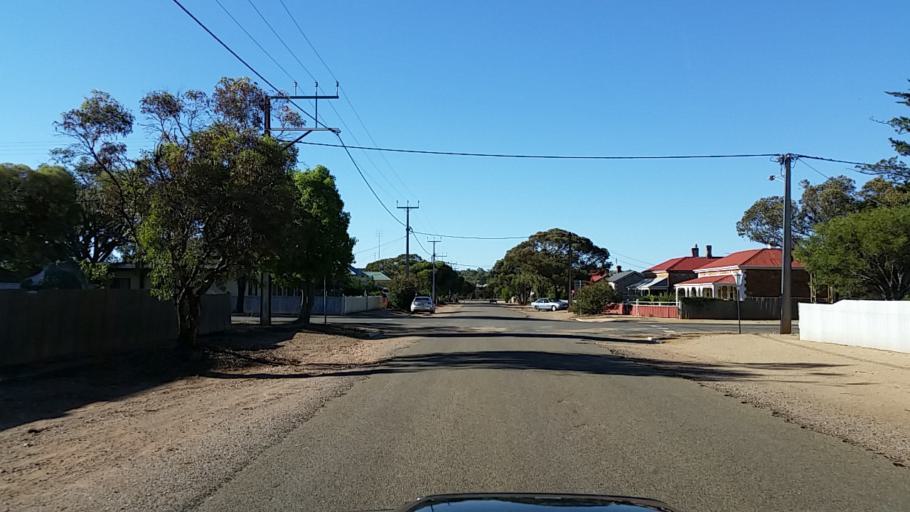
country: AU
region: South Australia
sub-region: Peterborough
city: Peterborough
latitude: -32.9772
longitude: 138.8374
